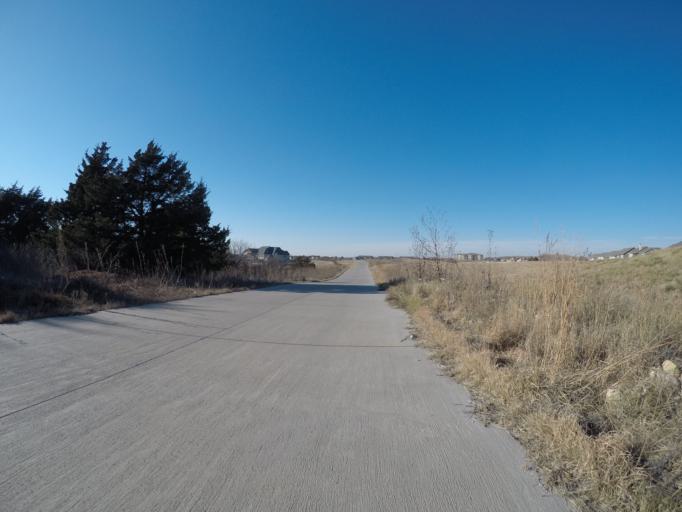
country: US
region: Kansas
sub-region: Riley County
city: Manhattan
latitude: 39.2038
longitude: -96.6450
